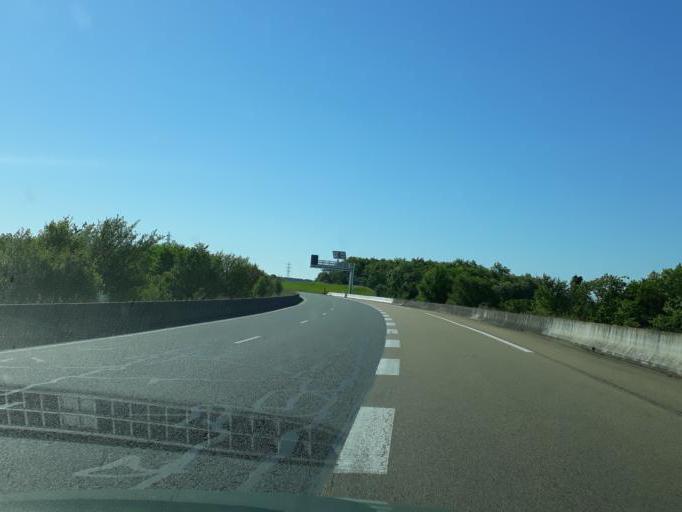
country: FR
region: Centre
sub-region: Departement du Loiret
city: Courtenay
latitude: 48.0492
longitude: 3.1063
